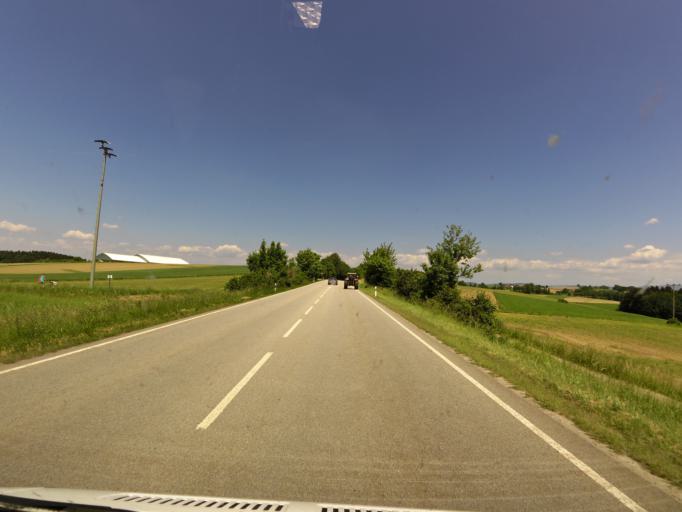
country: DE
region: Bavaria
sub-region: Lower Bavaria
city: Buchlberg
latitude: 48.6942
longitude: 13.5097
